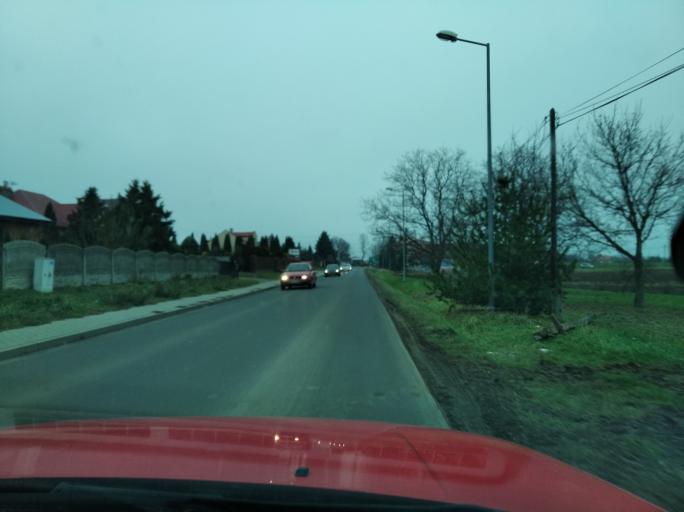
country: PL
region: Subcarpathian Voivodeship
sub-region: Powiat jaroslawski
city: Pawlosiow
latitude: 50.0132
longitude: 22.6468
